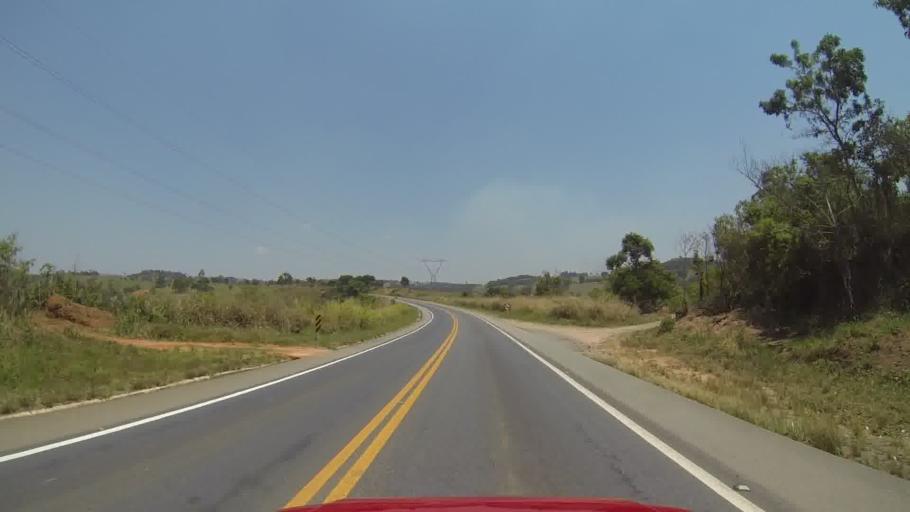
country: BR
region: Minas Gerais
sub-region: Itapecerica
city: Itapecerica
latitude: -20.3286
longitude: -45.2262
